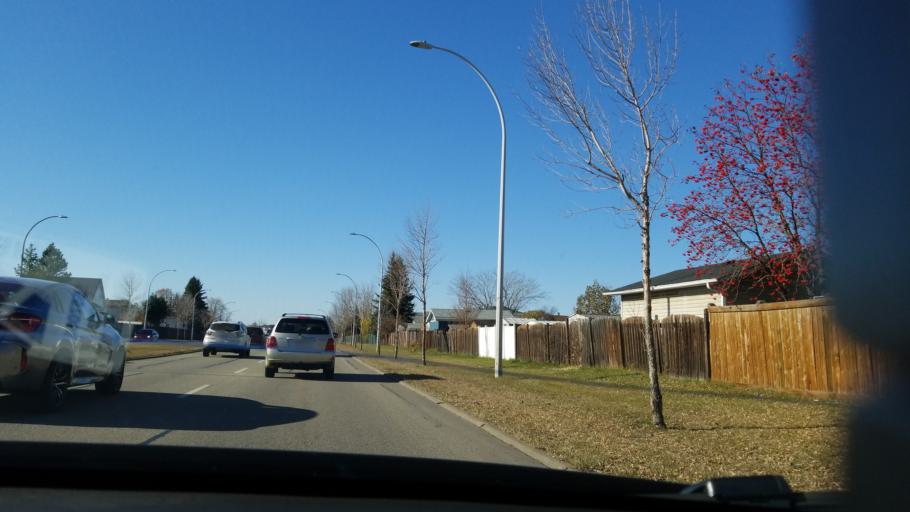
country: CA
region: Alberta
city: Edmonton
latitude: 53.6160
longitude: -113.4705
